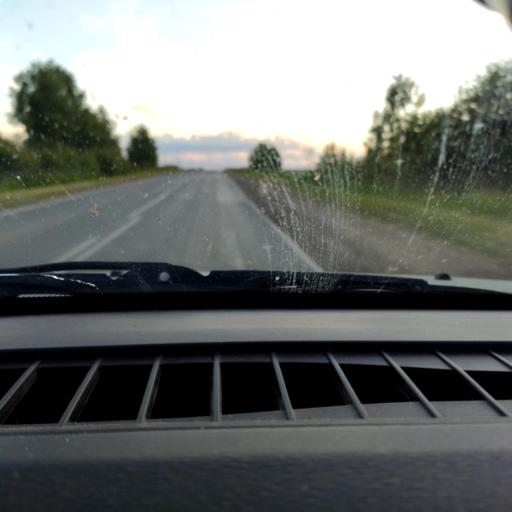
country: RU
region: Perm
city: Orda
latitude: 57.3345
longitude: 56.7469
